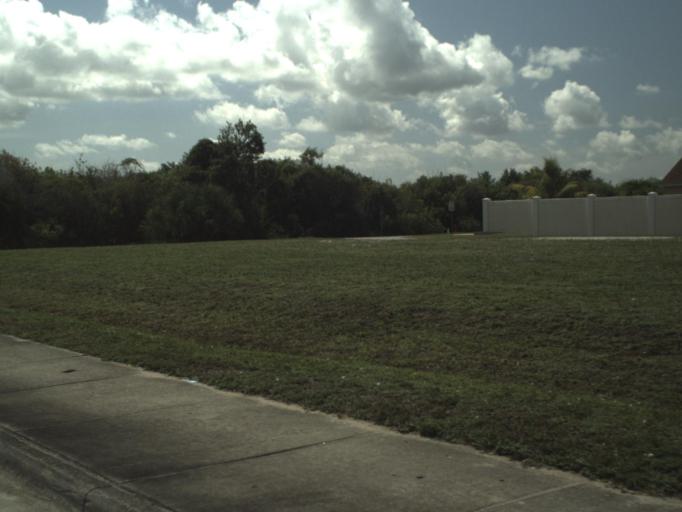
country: US
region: Florida
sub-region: Saint Lucie County
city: Port Saint Lucie
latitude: 27.2717
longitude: -80.3286
